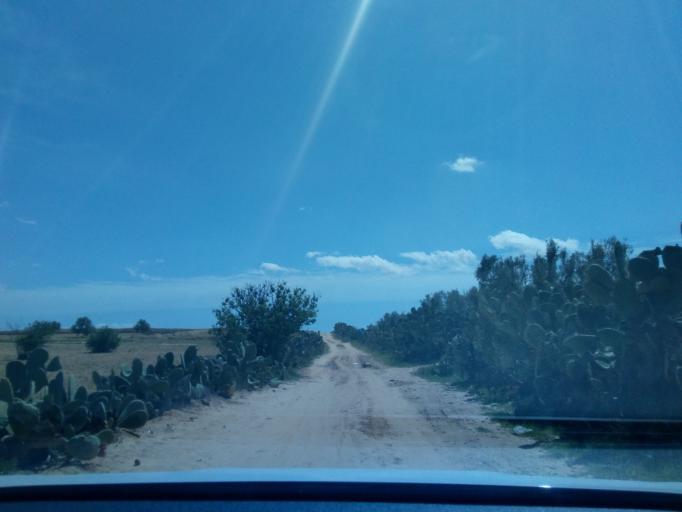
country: TN
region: Safaqis
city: Sfax
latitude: 34.7354
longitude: 10.4983
